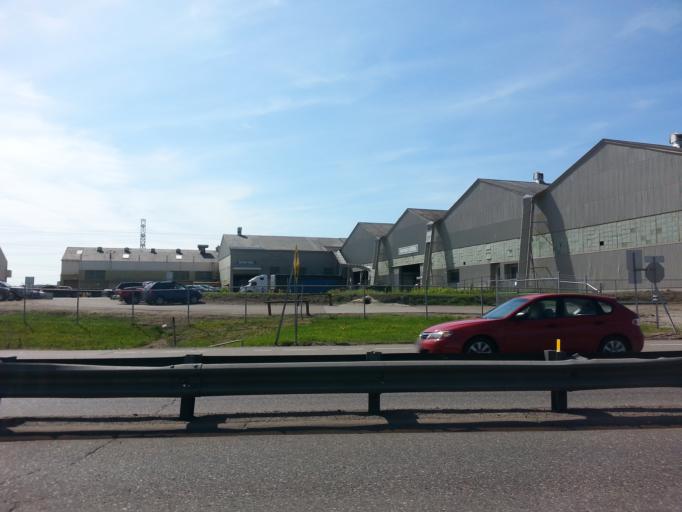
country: US
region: Minnesota
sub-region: Ramsey County
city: Lauderdale
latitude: 45.0027
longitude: -93.2047
